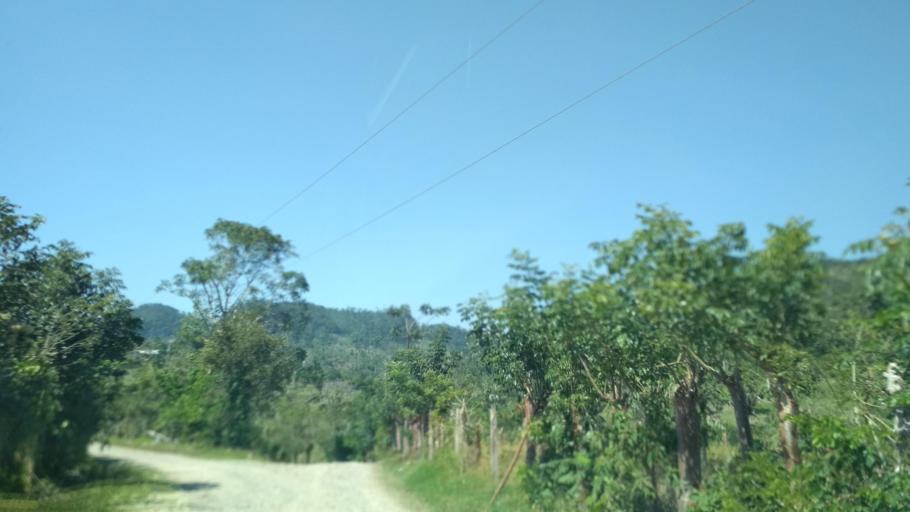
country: MX
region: Veracruz
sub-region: Papantla
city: Polutla
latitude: 20.4794
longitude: -97.2216
